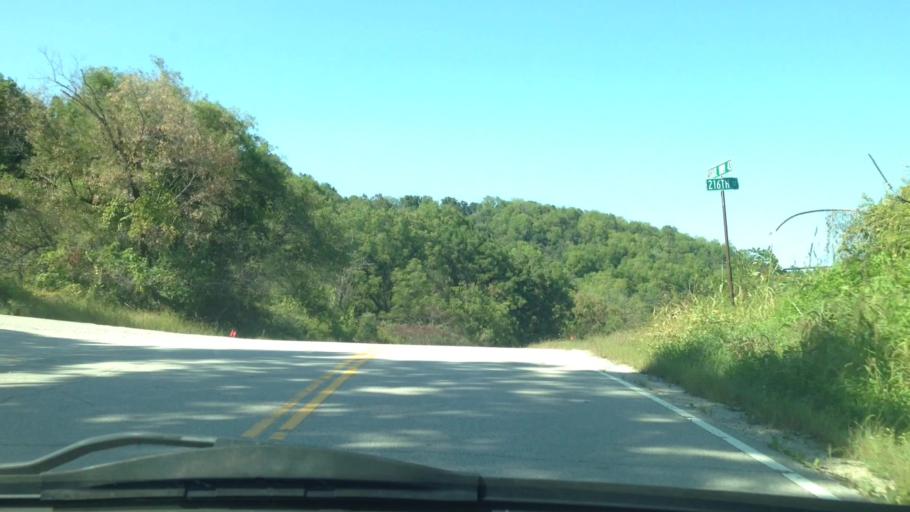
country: US
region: Minnesota
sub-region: Fillmore County
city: Rushford
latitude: 43.6668
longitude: -91.7939
